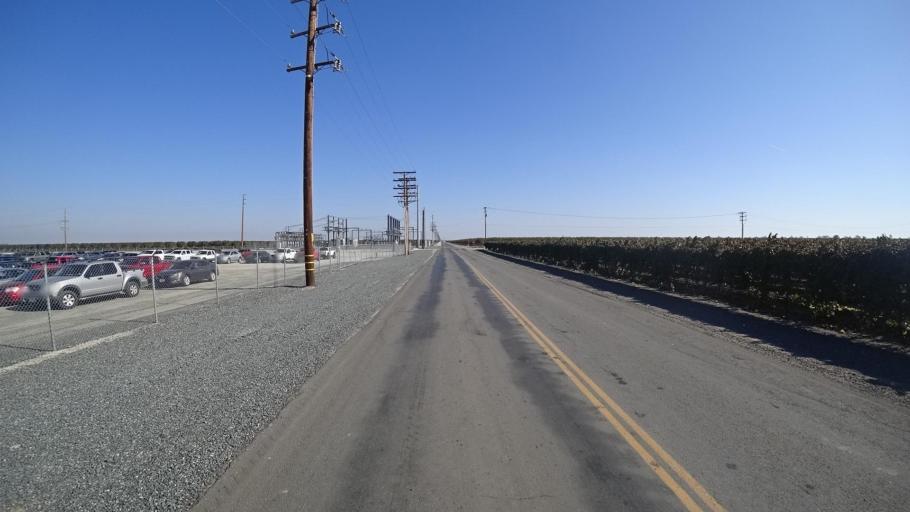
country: US
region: California
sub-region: Kern County
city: McFarland
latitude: 35.7034
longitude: -119.2060
